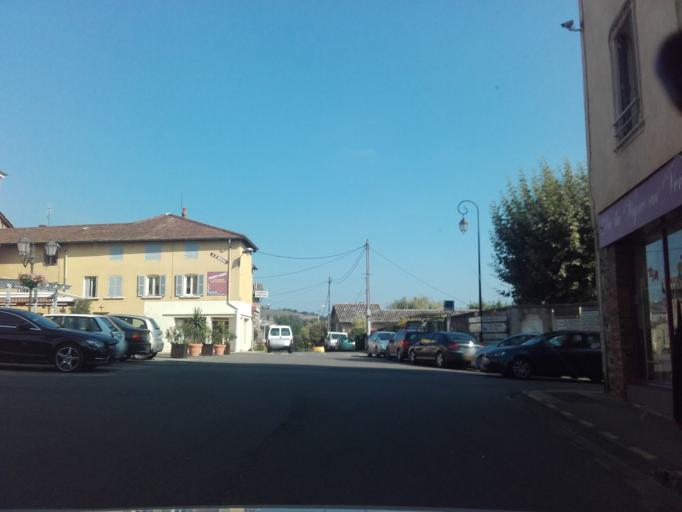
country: FR
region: Rhone-Alpes
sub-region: Departement du Rhone
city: Fleurie
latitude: 46.1925
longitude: 4.6973
